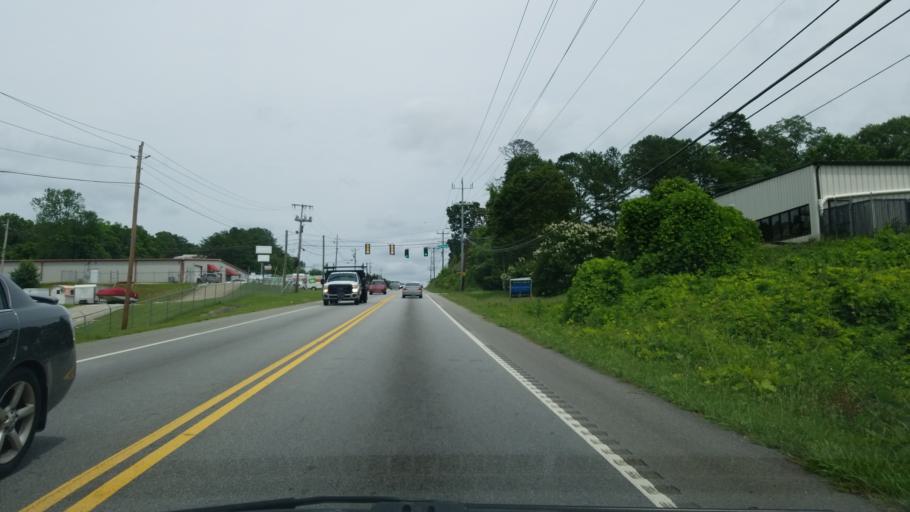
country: US
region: Tennessee
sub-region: Hamilton County
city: Harrison
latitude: 35.0744
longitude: -85.1718
